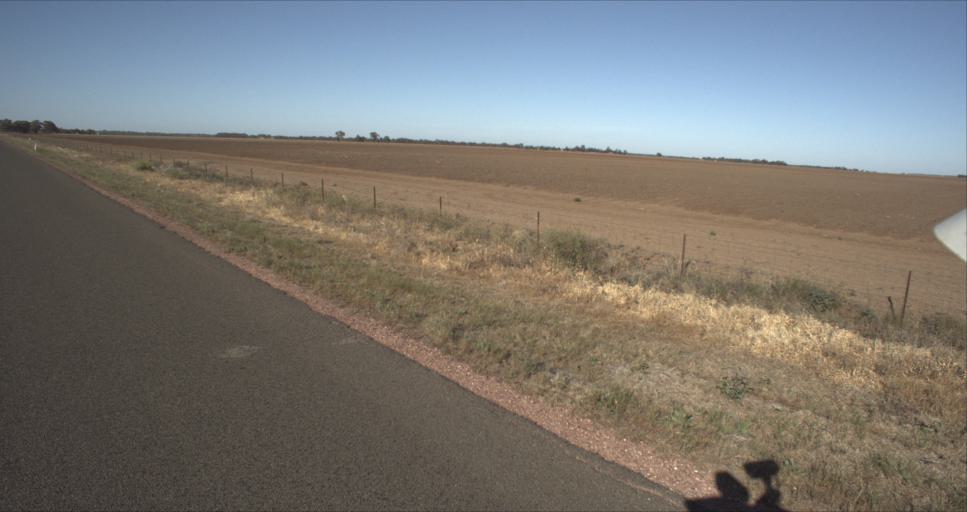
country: AU
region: New South Wales
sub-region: Leeton
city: Leeton
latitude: -34.5674
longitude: 146.2641
